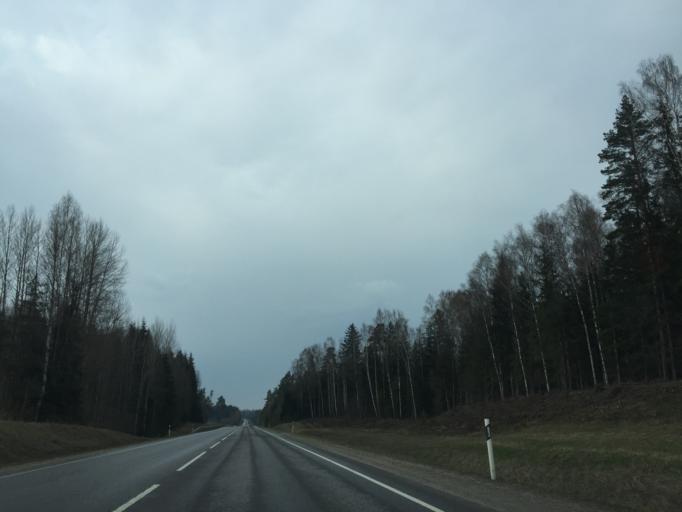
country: EE
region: Tartu
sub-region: UElenurme vald
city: Ulenurme
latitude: 58.1057
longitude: 26.7393
